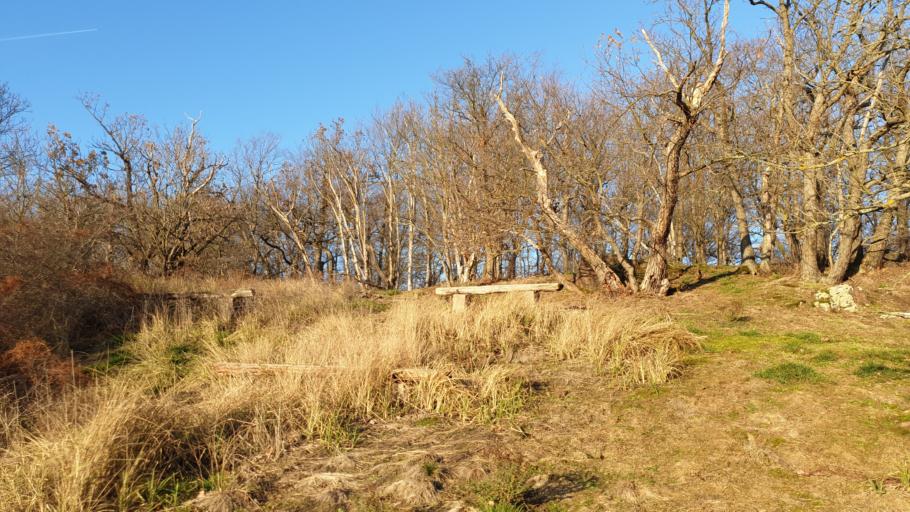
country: DE
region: Saxony
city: Hohburg
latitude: 51.4044
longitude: 12.7983
